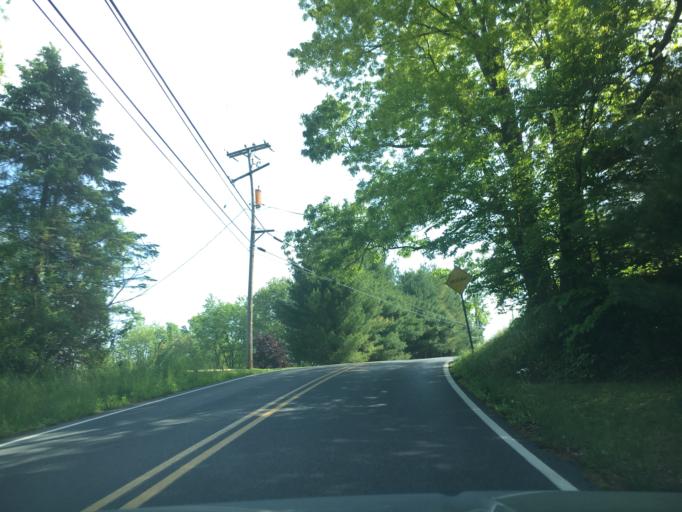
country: US
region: Pennsylvania
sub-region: Berks County
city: Boyertown
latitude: 40.3427
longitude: -75.6500
